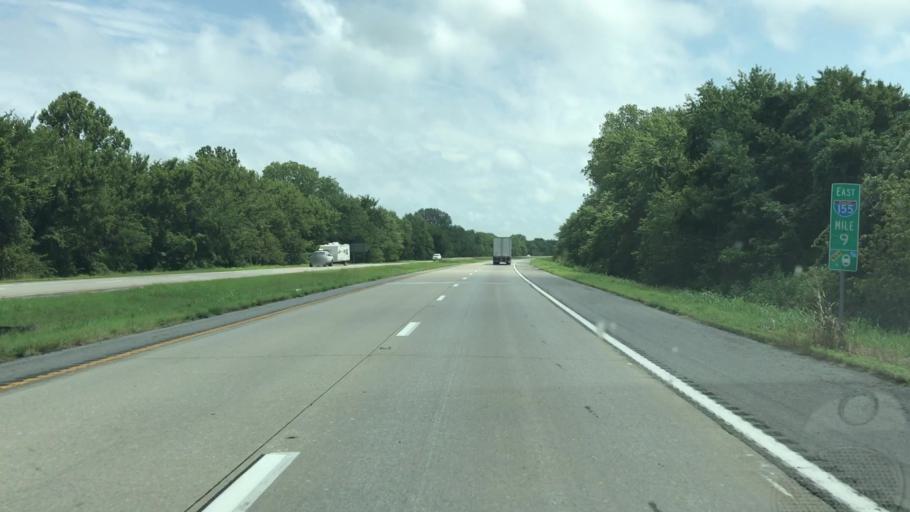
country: US
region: Missouri
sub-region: Pemiscot County
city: Caruthersville
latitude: 36.1339
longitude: -89.6269
